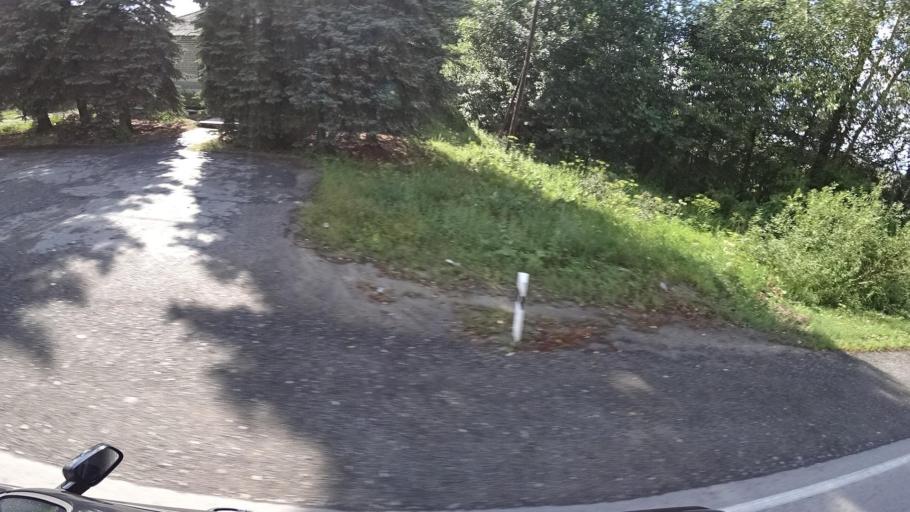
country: RU
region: Sverdlovsk
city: Kamyshlov
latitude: 56.8312
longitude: 62.6956
